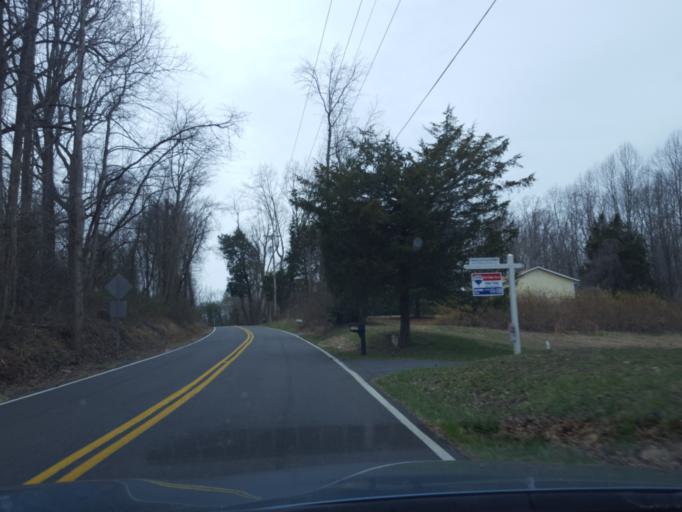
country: US
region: Maryland
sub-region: Calvert County
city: Prince Frederick
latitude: 38.4884
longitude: -76.5693
